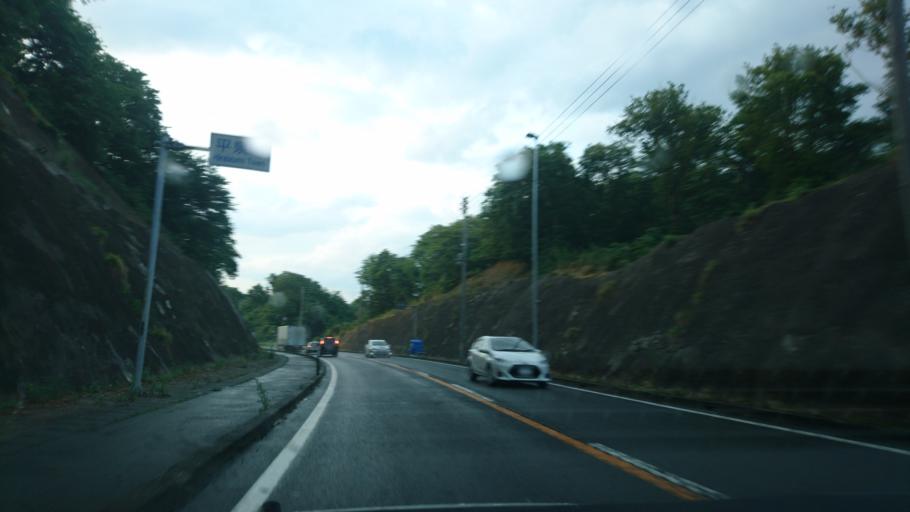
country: JP
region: Iwate
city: Ichinoseki
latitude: 38.9570
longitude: 141.1227
